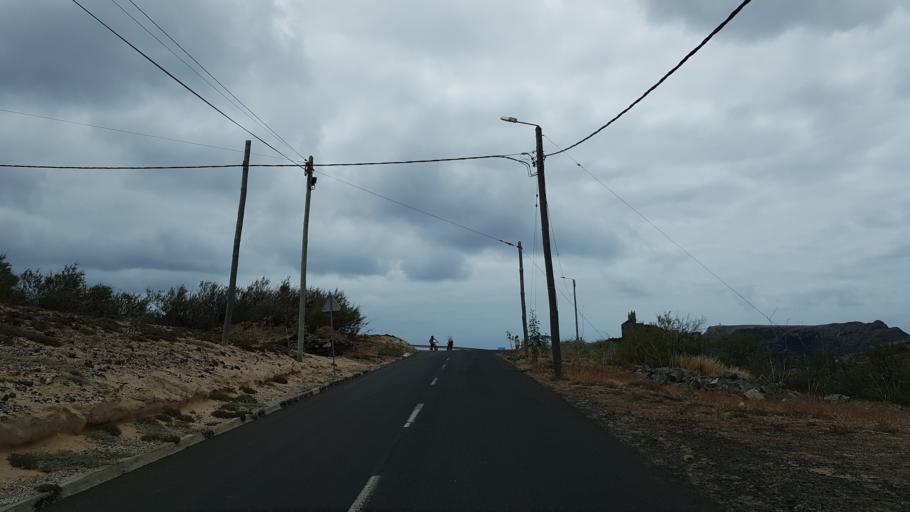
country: PT
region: Madeira
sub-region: Porto Santo
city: Vila de Porto Santo
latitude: 33.0702
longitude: -16.2992
